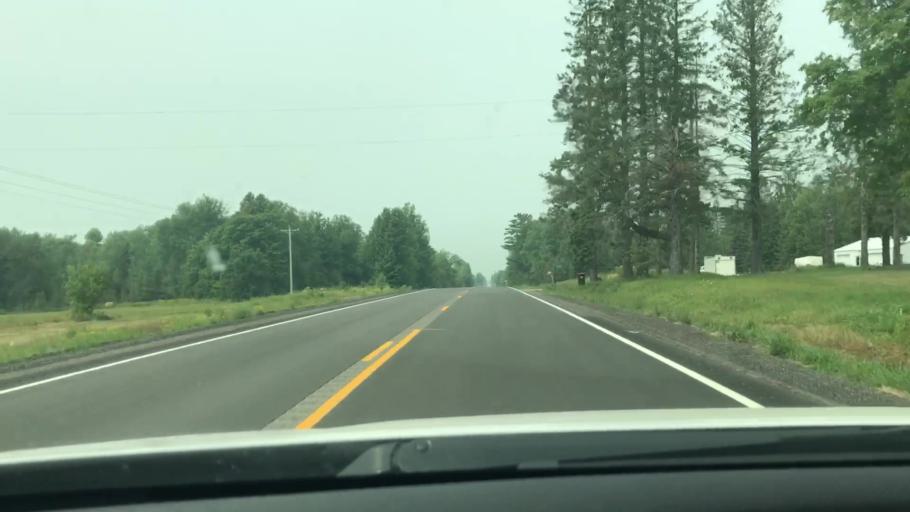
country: US
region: Minnesota
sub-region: Itasca County
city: Cohasset
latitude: 47.3595
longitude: -93.8604
